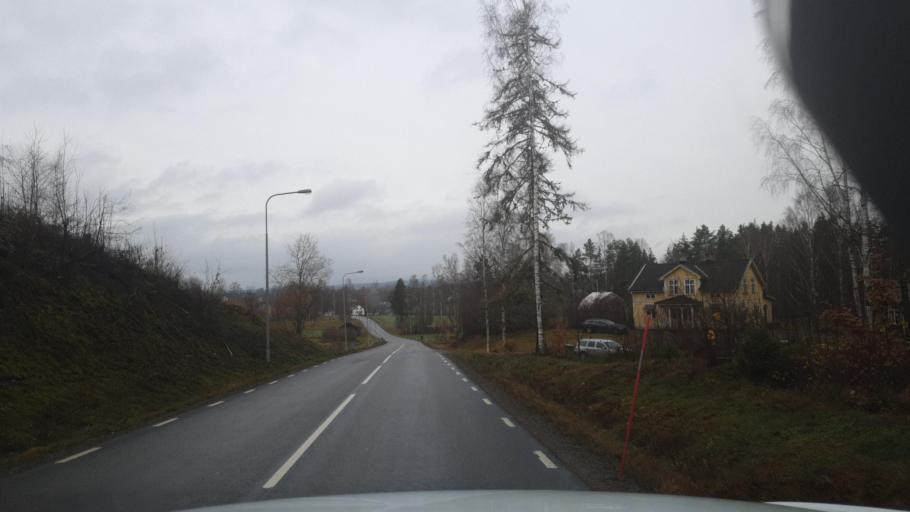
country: SE
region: Vaermland
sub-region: Arvika Kommun
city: Arvika
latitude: 59.5449
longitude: 12.5727
